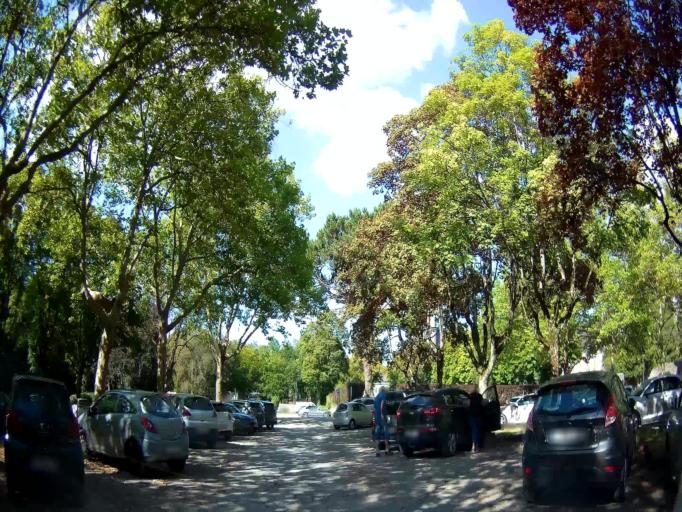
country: BE
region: Wallonia
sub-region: Province de Namur
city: Onhaye
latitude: 50.3010
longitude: 4.7652
